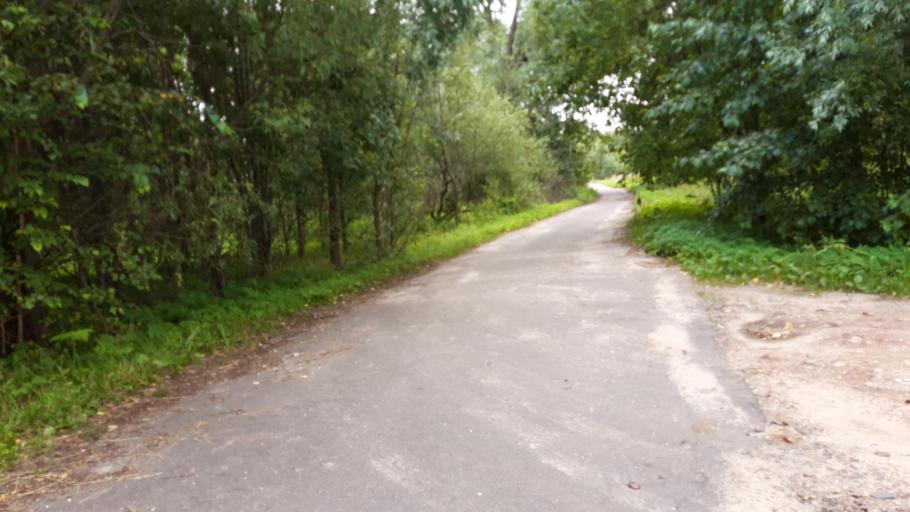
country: RU
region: Tverskaya
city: Konakovo
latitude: 56.6837
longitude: 36.6982
